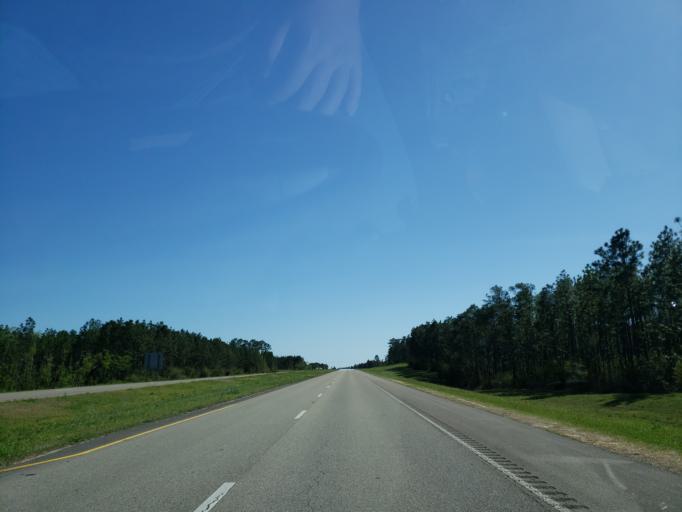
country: US
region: Mississippi
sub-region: Harrison County
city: Lyman
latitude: 30.5344
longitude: -89.0318
